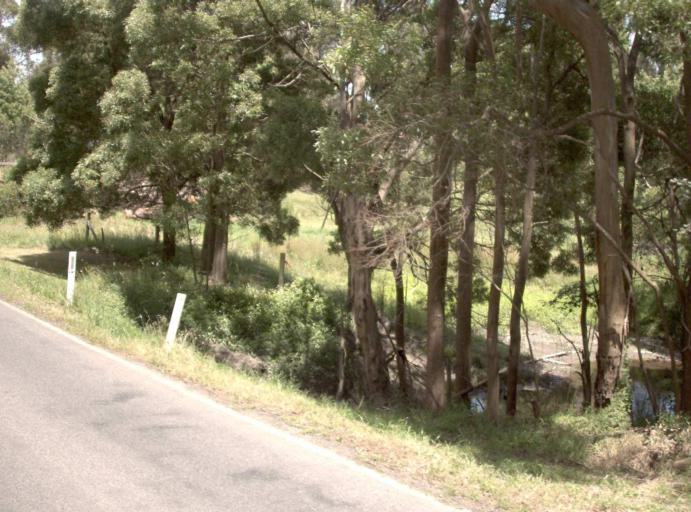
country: AU
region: Victoria
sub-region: Bass Coast
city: North Wonthaggi
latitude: -38.6037
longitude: 146.0185
